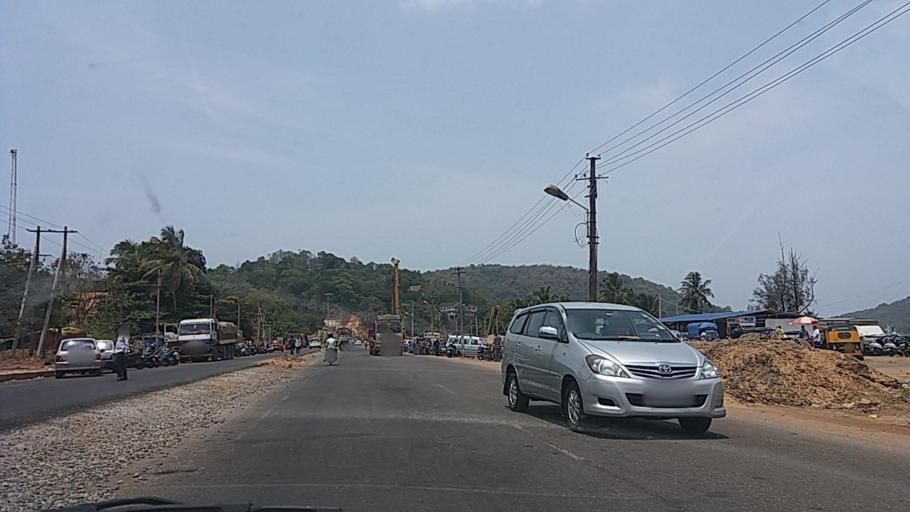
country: IN
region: Karnataka
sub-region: Uttar Kannada
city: Karwar
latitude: 14.8088
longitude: 74.1267
